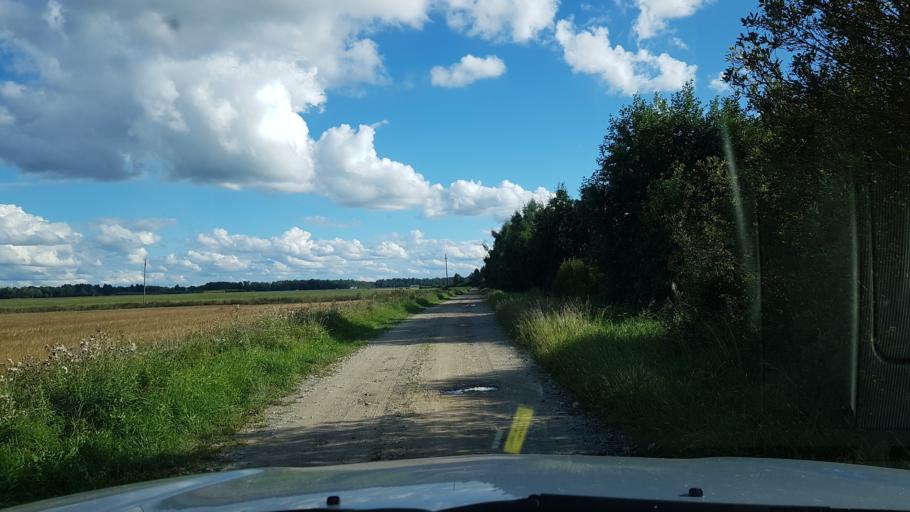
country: EE
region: Harju
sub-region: Rae vald
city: Jueri
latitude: 59.3567
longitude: 24.8552
